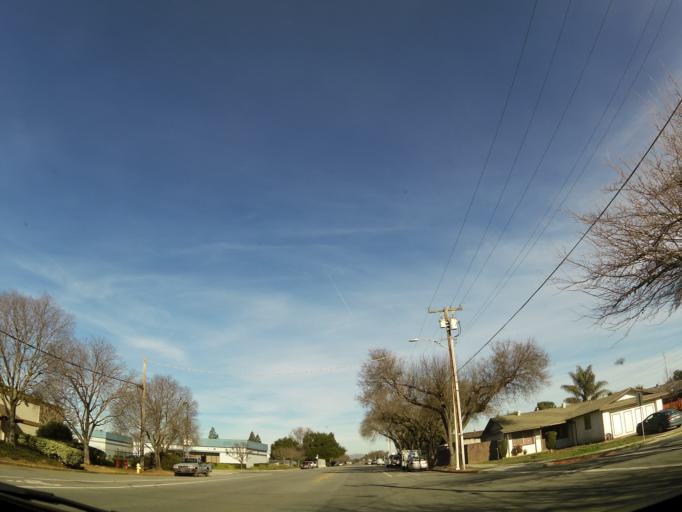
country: US
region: California
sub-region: Santa Clara County
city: Gilroy
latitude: 37.0268
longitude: -121.5720
